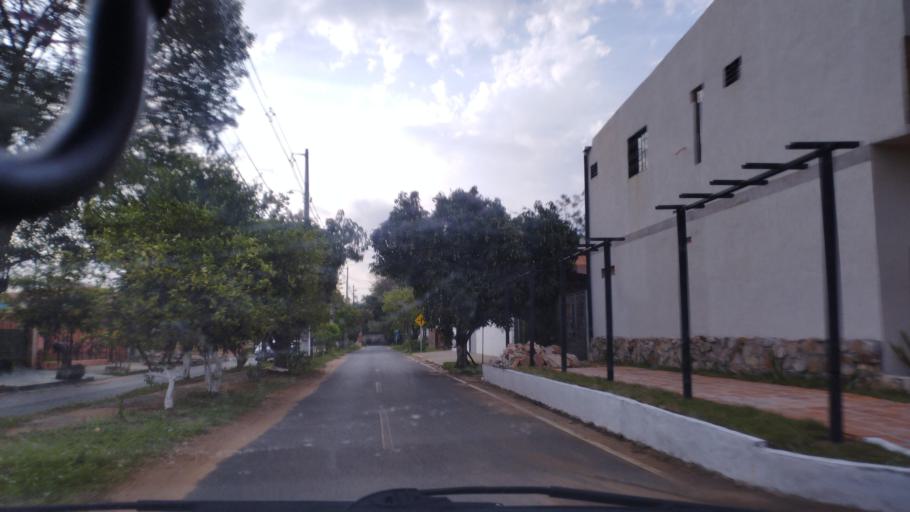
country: PY
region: Central
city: Fernando de la Mora
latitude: -25.3024
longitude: -57.5189
